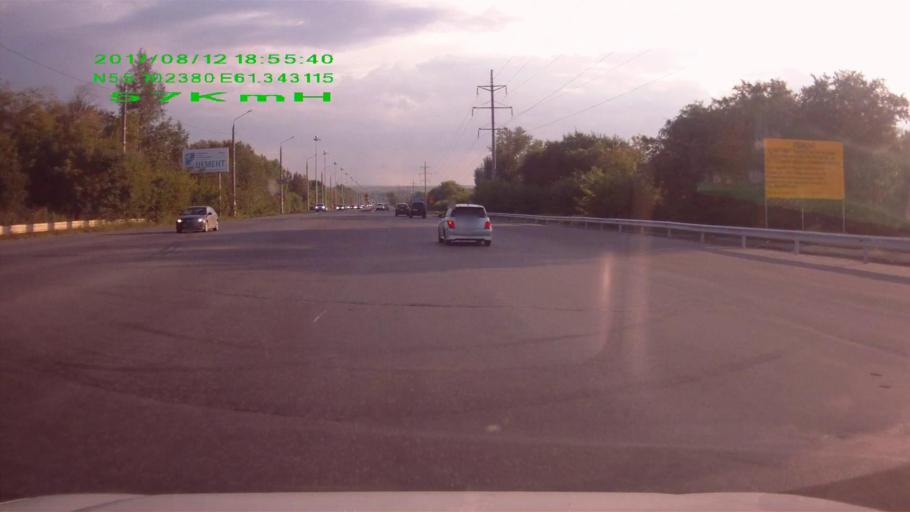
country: RU
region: Chelyabinsk
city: Novosineglazovskiy
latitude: 55.0961
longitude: 61.3345
